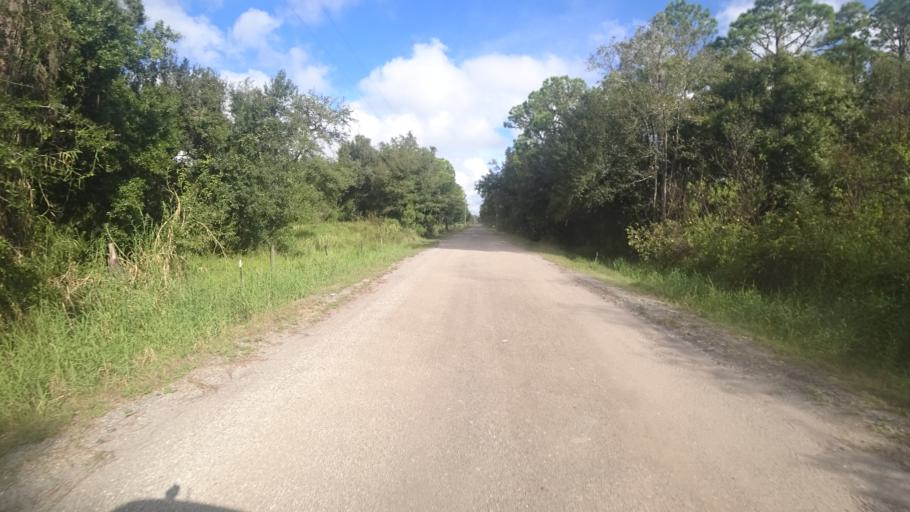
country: US
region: Florida
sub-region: Hillsborough County
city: Sun City Center
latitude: 27.5974
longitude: -82.3638
